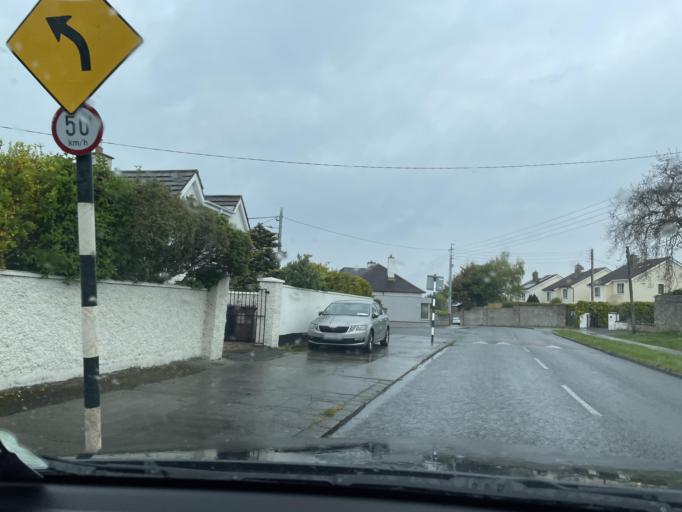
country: IE
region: Leinster
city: Dundrum
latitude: 53.2887
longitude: -6.2565
